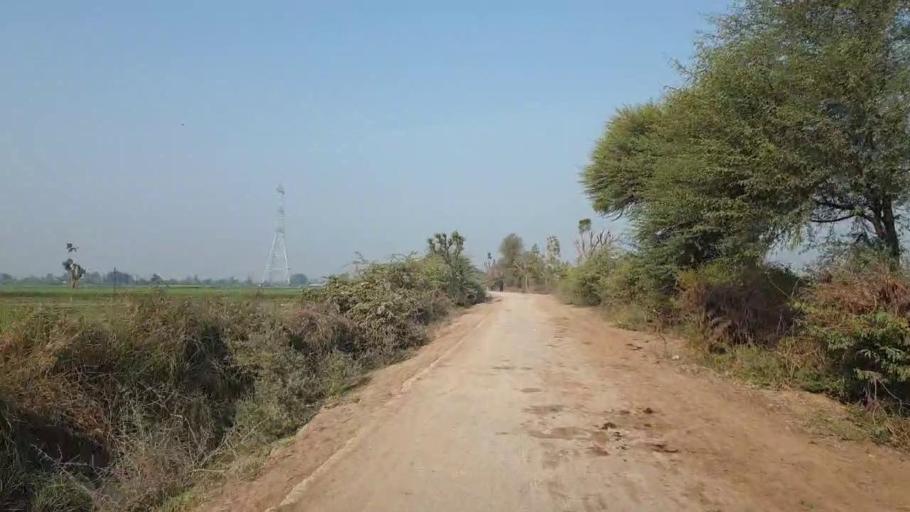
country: PK
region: Sindh
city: Matiari
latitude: 25.6767
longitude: 68.4969
